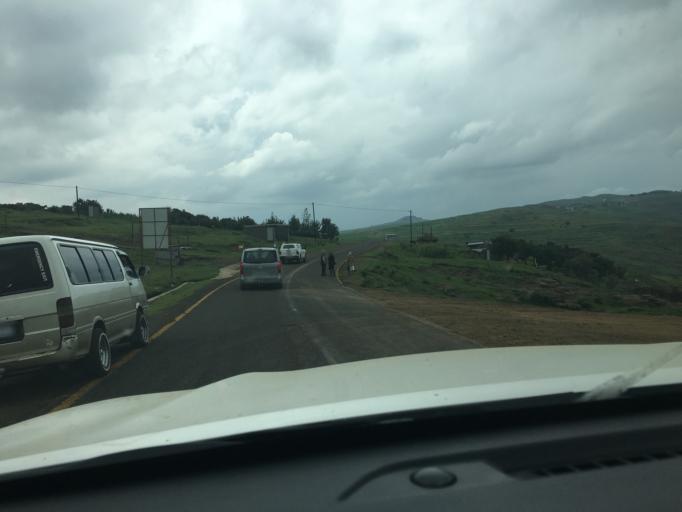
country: LS
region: Berea
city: Teyateyaneng
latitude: -29.2541
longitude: 27.8465
